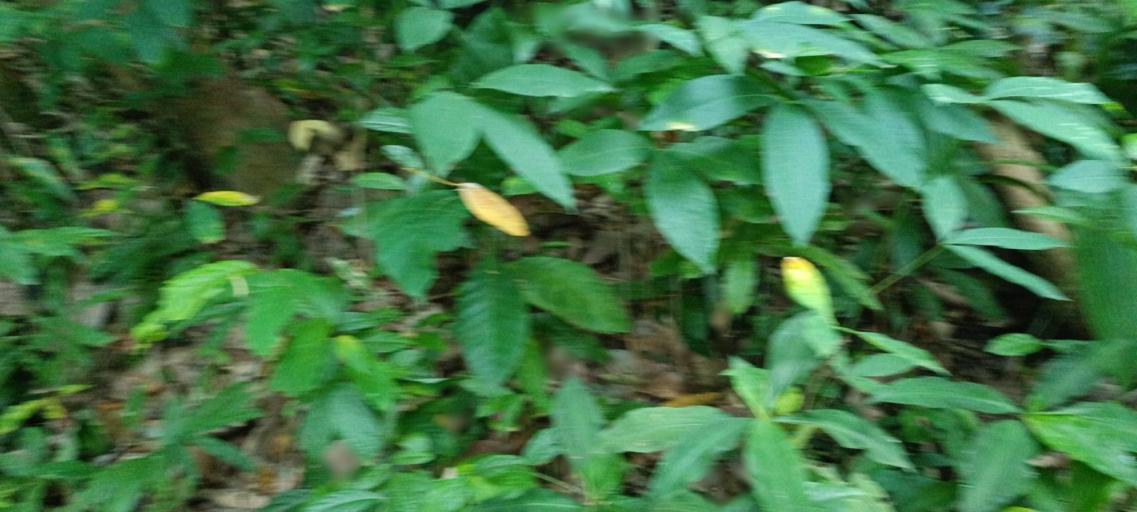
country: MY
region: Penang
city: Kampung Sungai Ara
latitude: 5.3456
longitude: 100.2833
